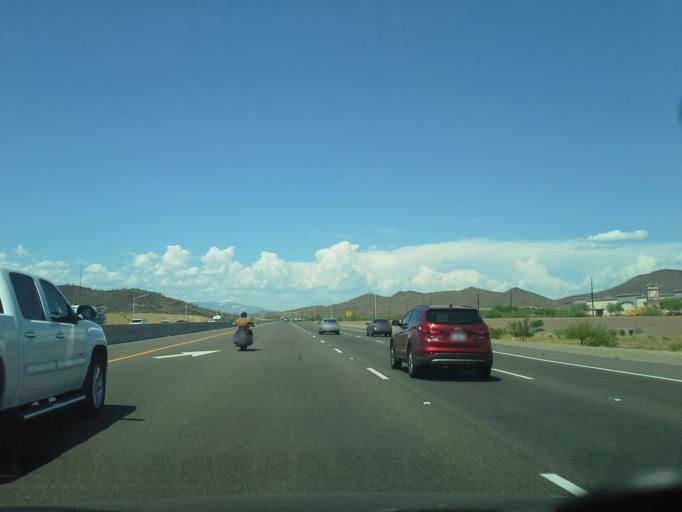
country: US
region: Arizona
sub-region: Maricopa County
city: Anthem
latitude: 33.7992
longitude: -112.1356
